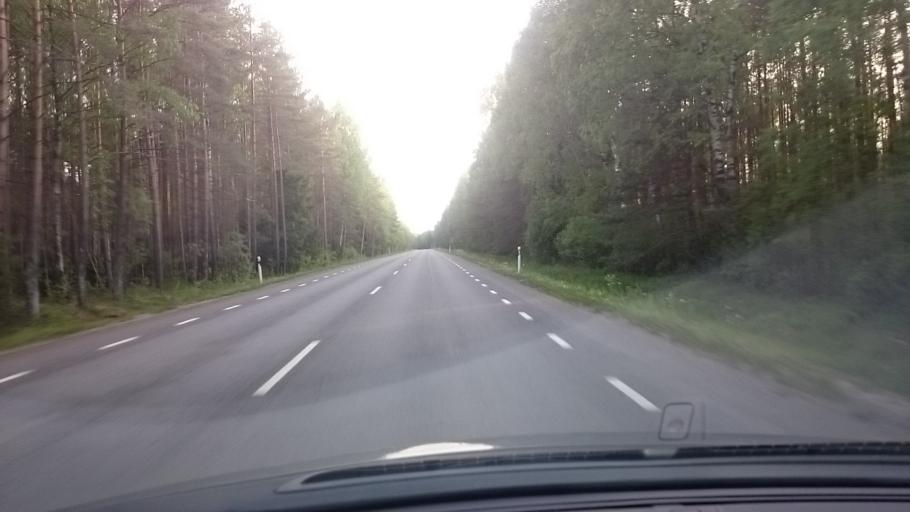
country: EE
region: Viljandimaa
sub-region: Viiratsi vald
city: Viiratsi
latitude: 58.4725
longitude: 25.7804
